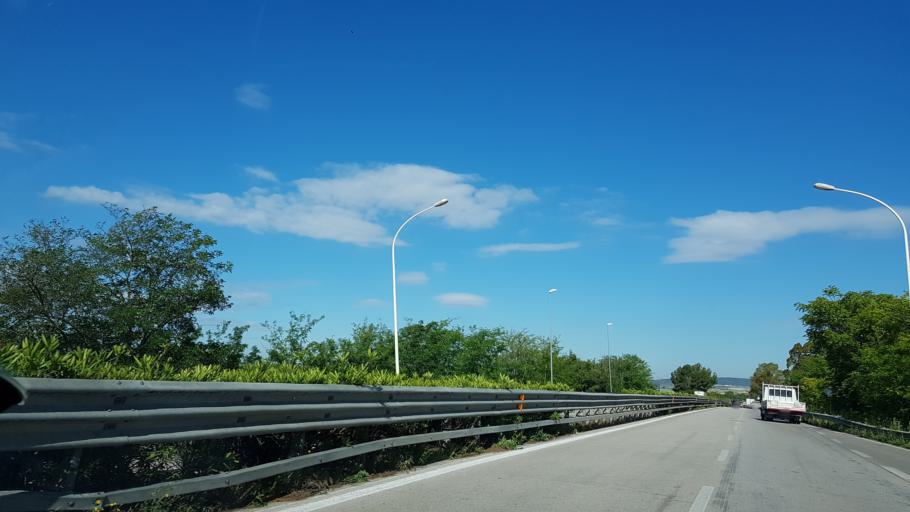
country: IT
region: Apulia
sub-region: Provincia di Taranto
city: Grottaglie
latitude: 40.5270
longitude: 17.4181
